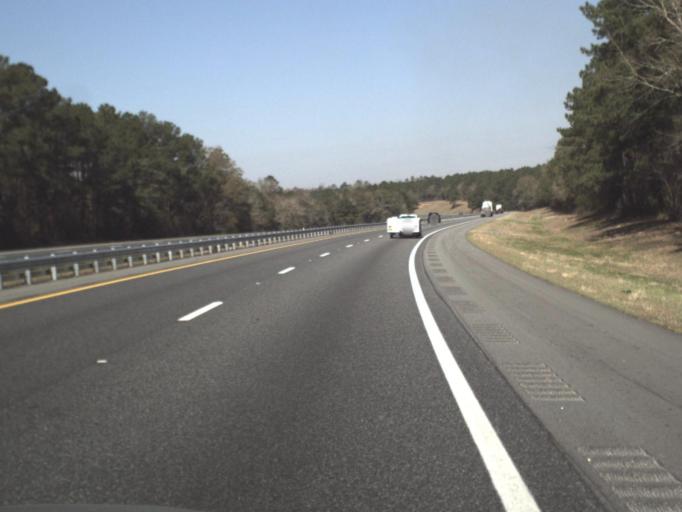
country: US
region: Florida
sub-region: Gadsden County
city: Gretna
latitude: 30.6061
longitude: -84.7399
